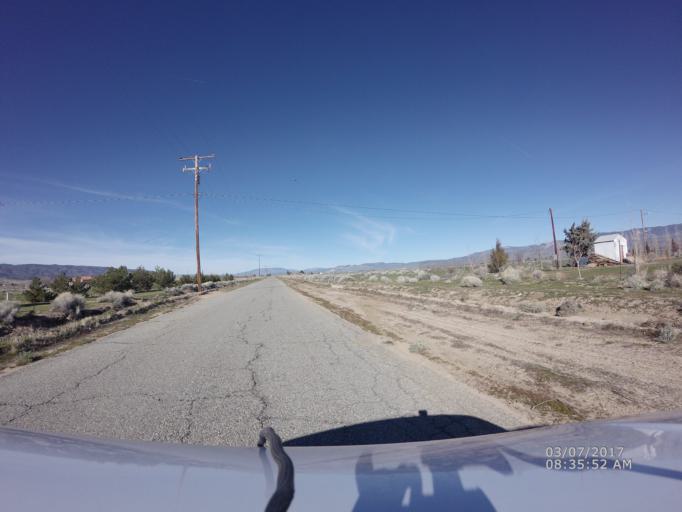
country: US
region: California
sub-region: Los Angeles County
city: Green Valley
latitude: 34.7892
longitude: -118.5377
